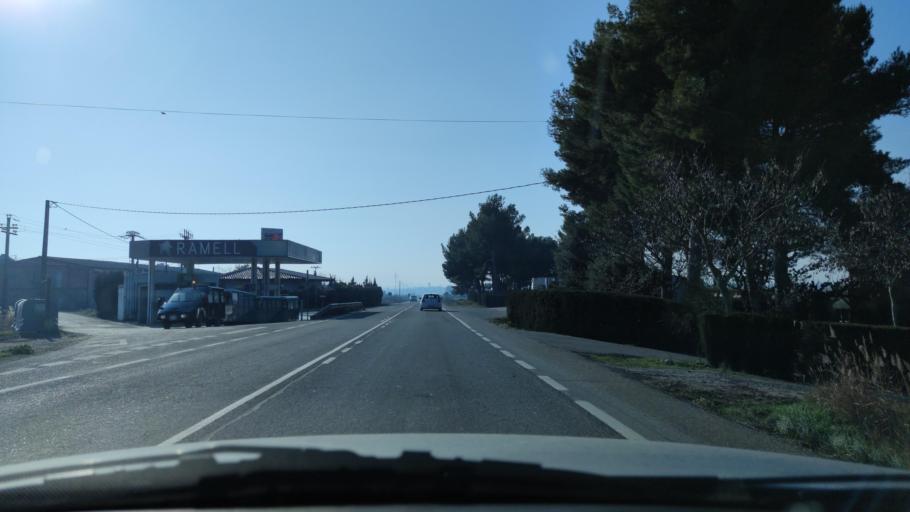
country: ES
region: Catalonia
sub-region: Provincia de Lleida
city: Torrefarrera
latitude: 41.6884
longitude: 0.6329
